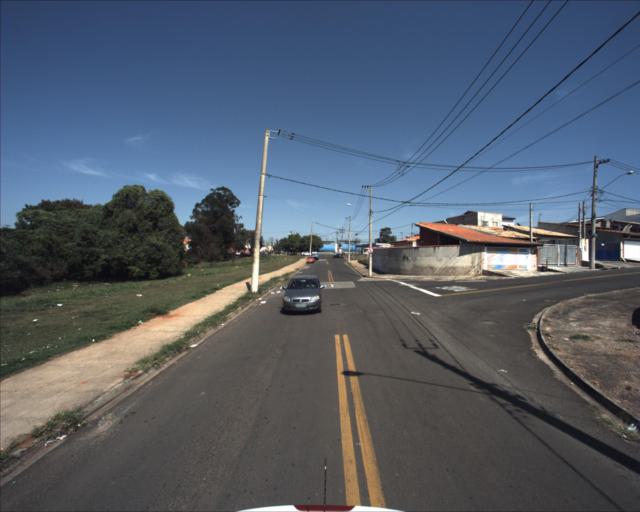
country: BR
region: Sao Paulo
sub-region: Sorocaba
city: Sorocaba
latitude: -23.4667
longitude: -47.4927
